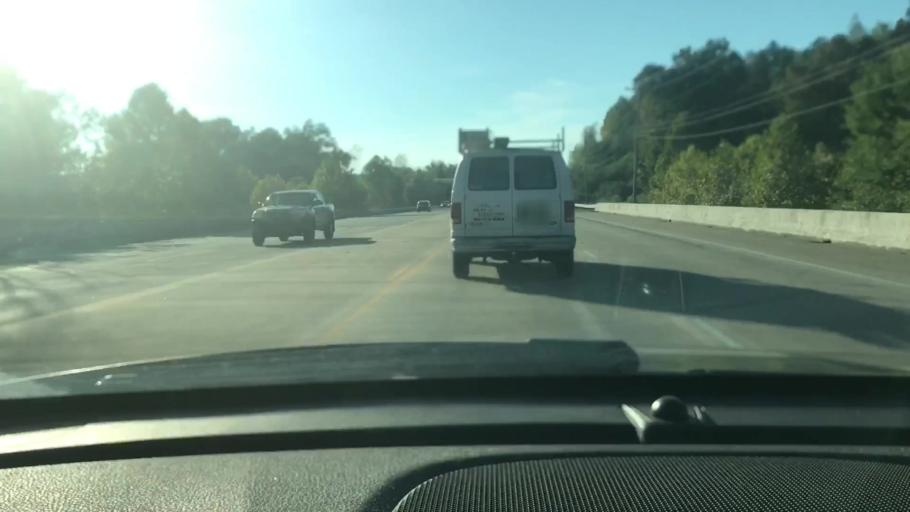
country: US
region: Tennessee
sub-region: Cheatham County
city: Ashland City
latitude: 36.2610
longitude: -87.0492
